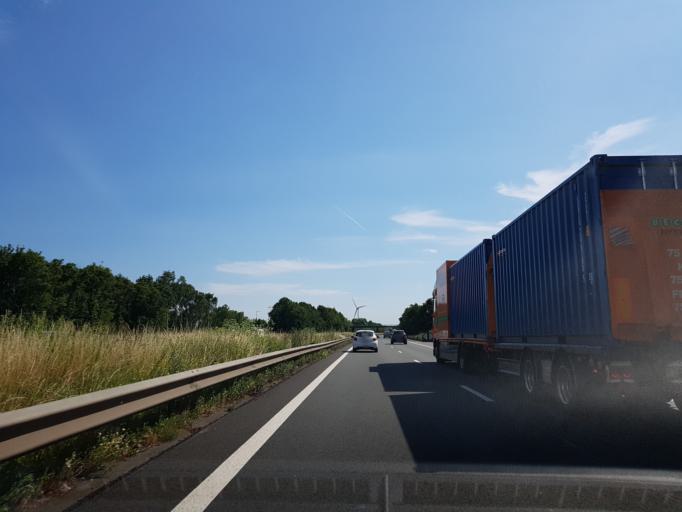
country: FR
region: Nord-Pas-de-Calais
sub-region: Departement du Nord
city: Onnaing
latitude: 50.3837
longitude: 3.6110
